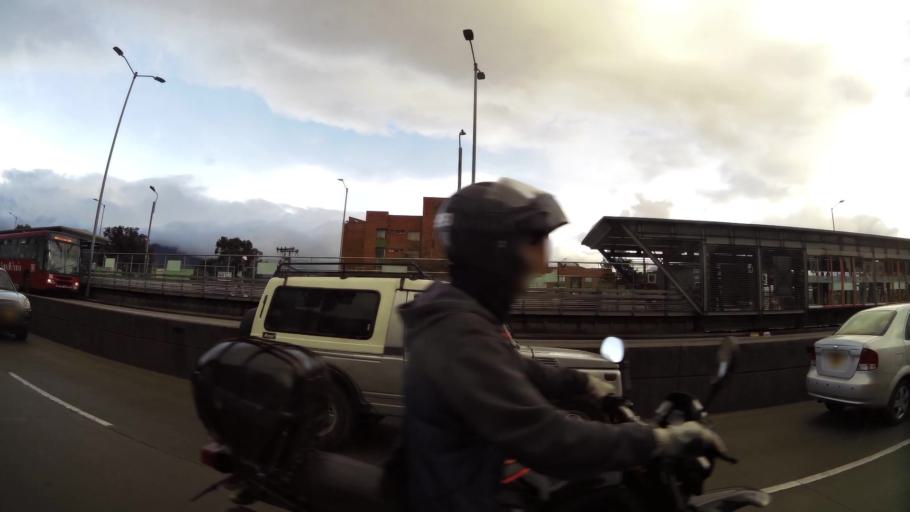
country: CO
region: Bogota D.C.
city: Bogota
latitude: 4.5974
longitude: -74.1109
